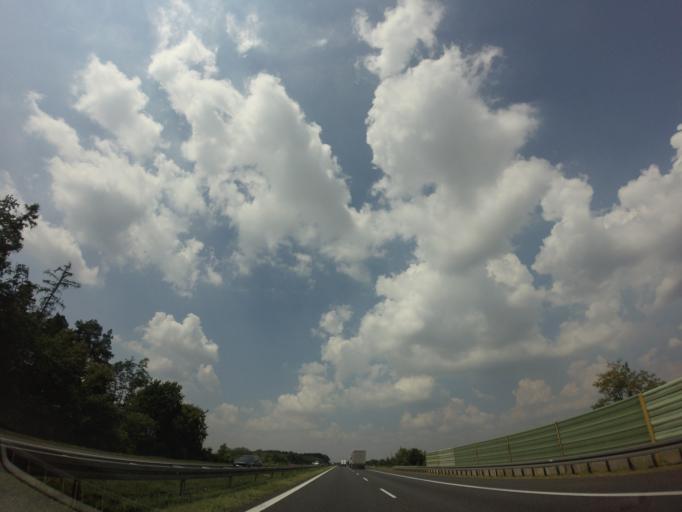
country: PL
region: Silesian Voivodeship
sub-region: Powiat gliwicki
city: Rudziniec
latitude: 50.3734
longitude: 18.4854
